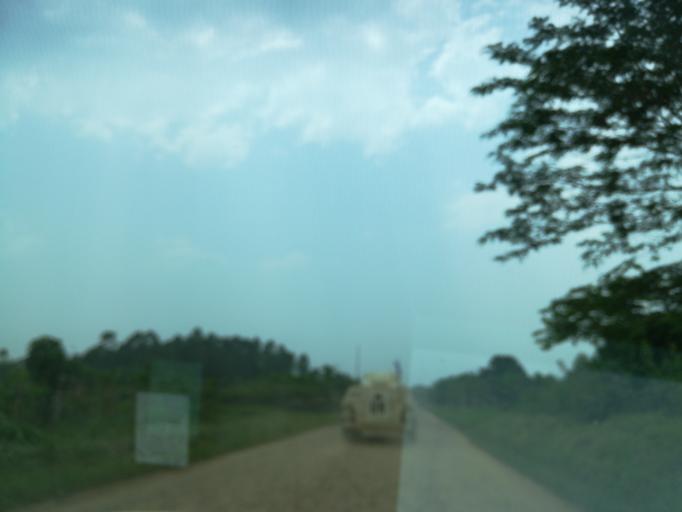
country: UG
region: Western Region
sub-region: Kasese District
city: Margherita
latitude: 0.3118
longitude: 29.6706
